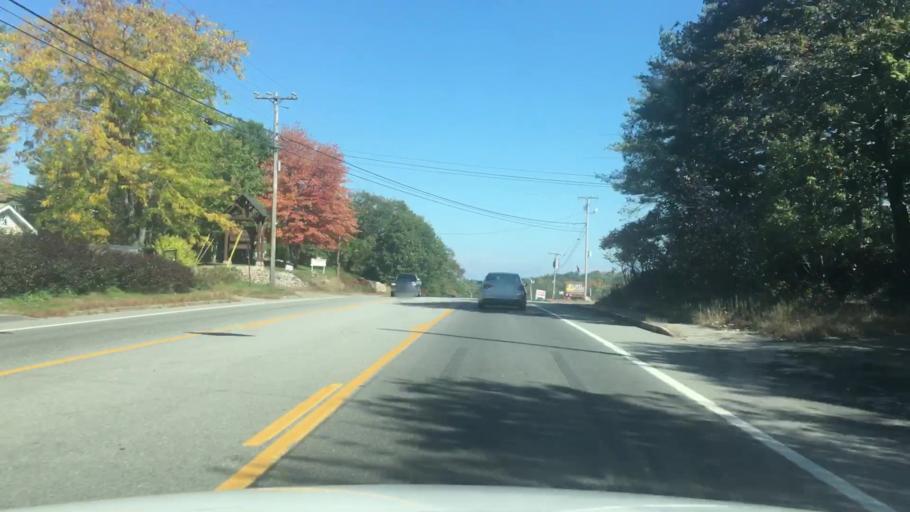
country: US
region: Maine
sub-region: Sagadahoc County
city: Woolwich
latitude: 43.9200
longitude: -69.7998
